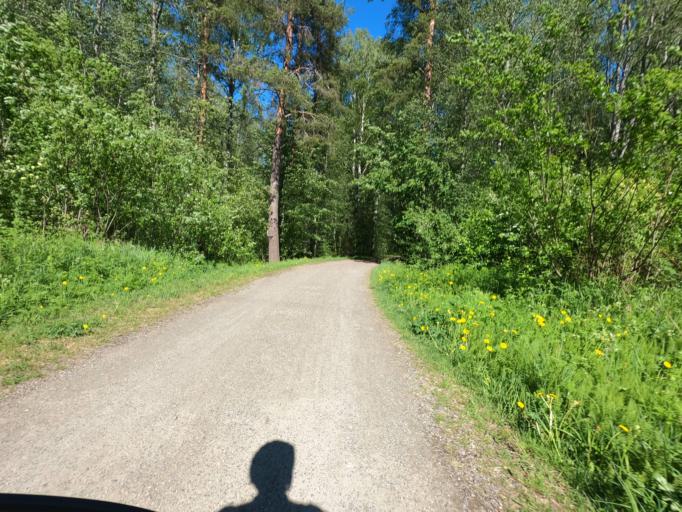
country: FI
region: North Karelia
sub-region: Joensuu
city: Joensuu
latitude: 62.6059
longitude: 29.7841
